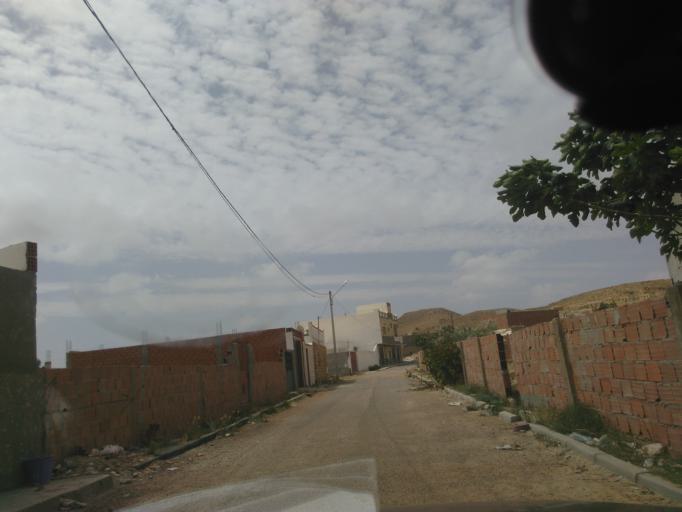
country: TN
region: Tataouine
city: Tataouine
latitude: 32.9469
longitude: 10.4712
